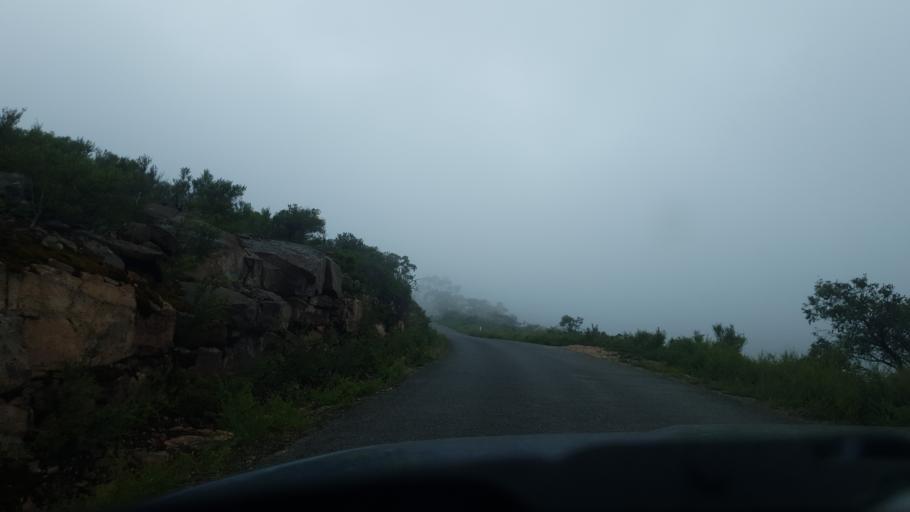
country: AU
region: Victoria
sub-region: Northern Grampians
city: Stawell
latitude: -37.2732
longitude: 142.5809
